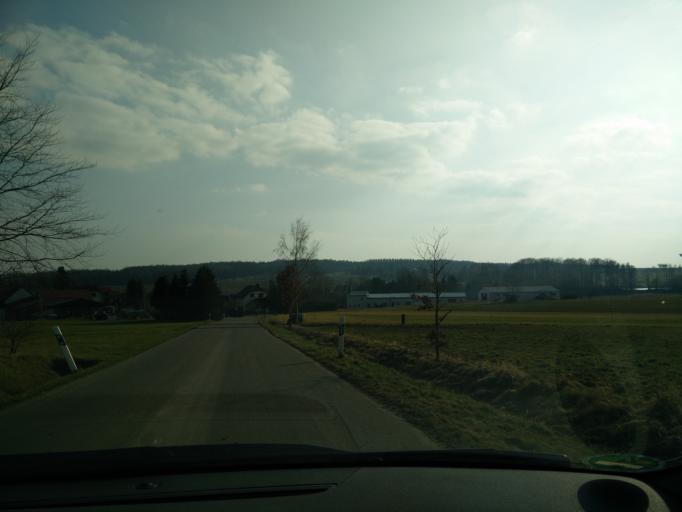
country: DE
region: Saxony
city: Konigsfeld
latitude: 51.0928
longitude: 12.7284
